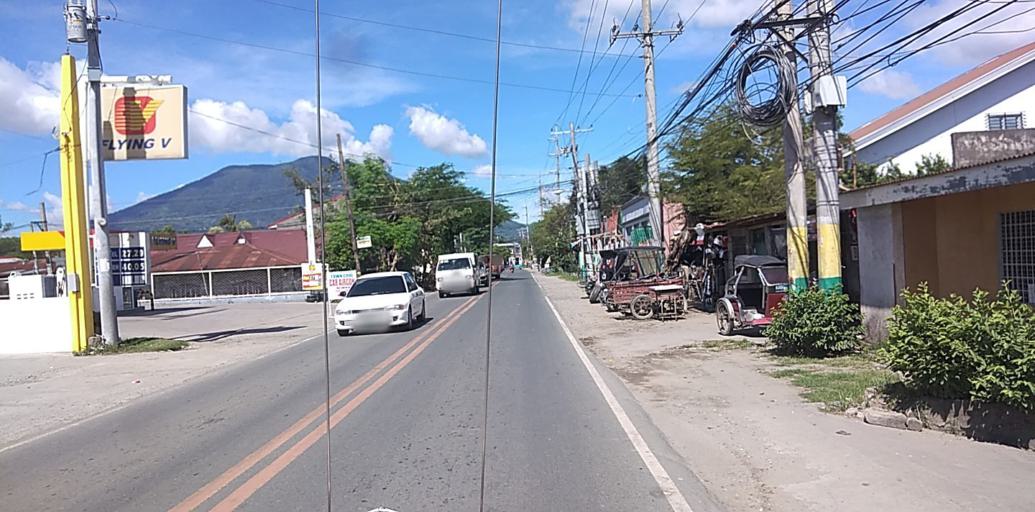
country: PH
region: Central Luzon
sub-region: Province of Pampanga
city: Arayat
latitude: 15.1387
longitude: 120.7731
